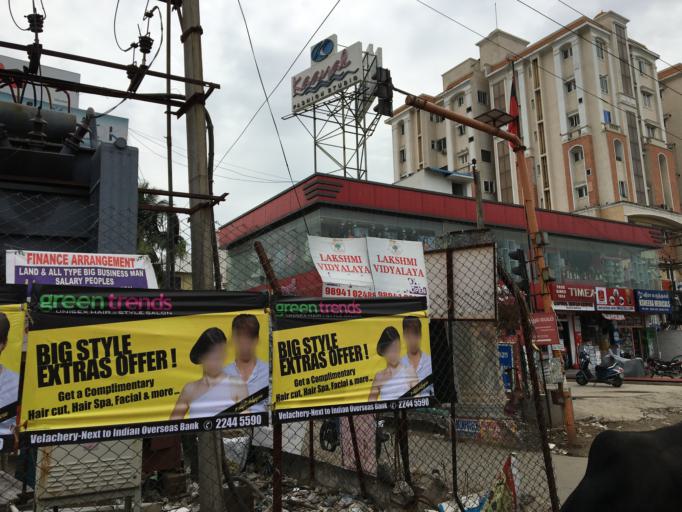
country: IN
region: Tamil Nadu
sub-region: Kancheepuram
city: Alandur
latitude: 12.9823
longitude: 80.2179
